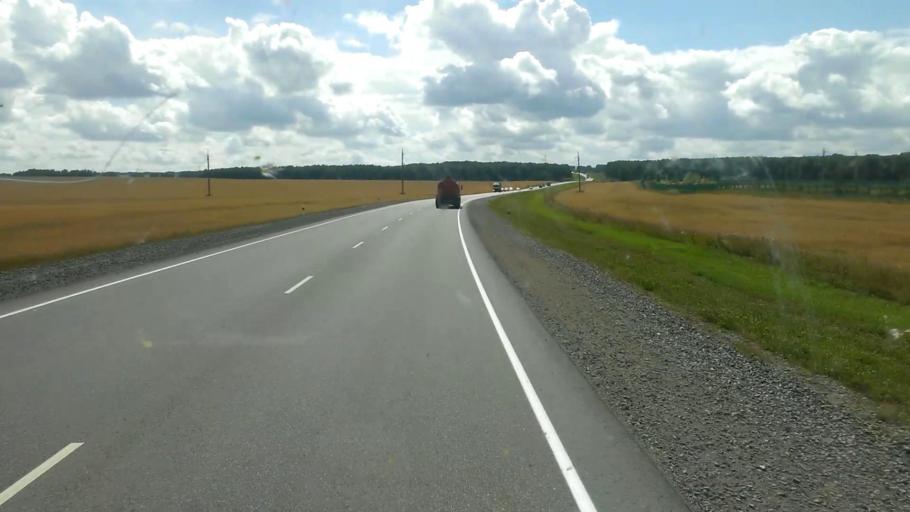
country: RU
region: Altai Krai
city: Troitskoye
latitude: 52.9924
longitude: 84.7416
